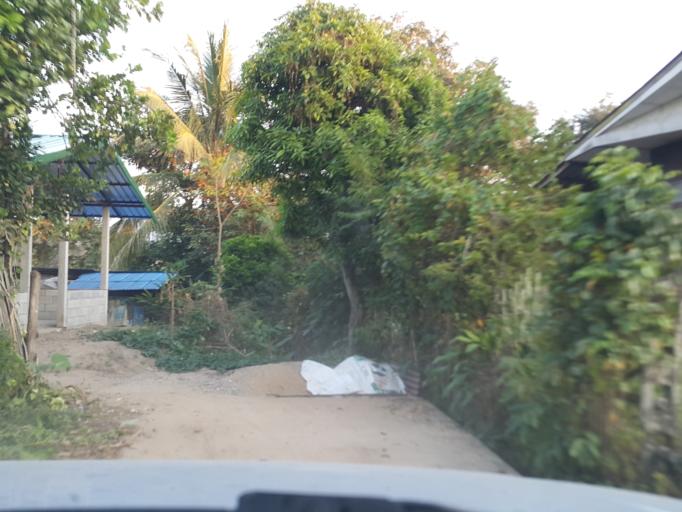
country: TH
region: Lamphun
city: Ban Thi
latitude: 18.5984
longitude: 99.2723
